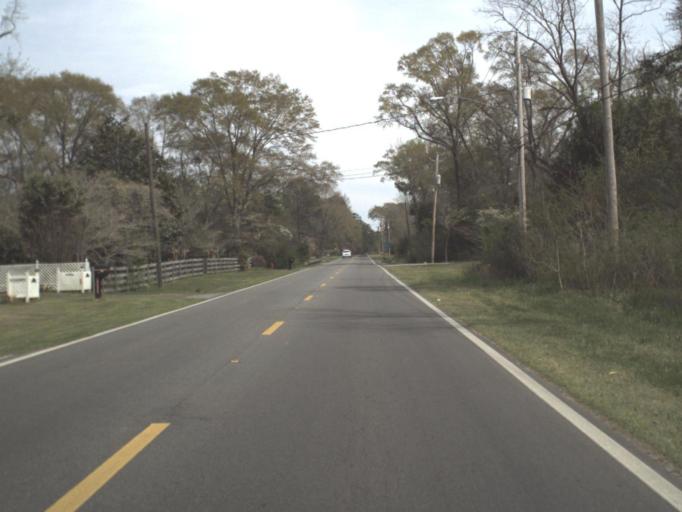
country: US
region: Florida
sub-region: Jackson County
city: Graceville
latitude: 30.9572
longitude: -85.5090
